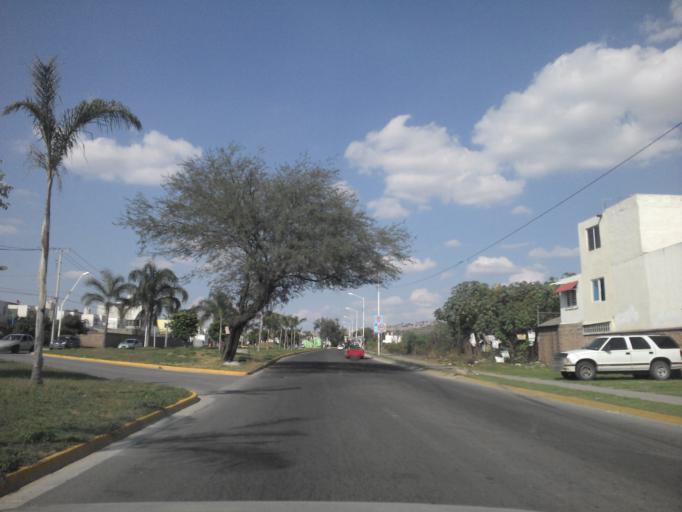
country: MX
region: Jalisco
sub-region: San Pedro Tlaquepaque
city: Paseo del Prado
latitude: 20.5769
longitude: -103.3883
